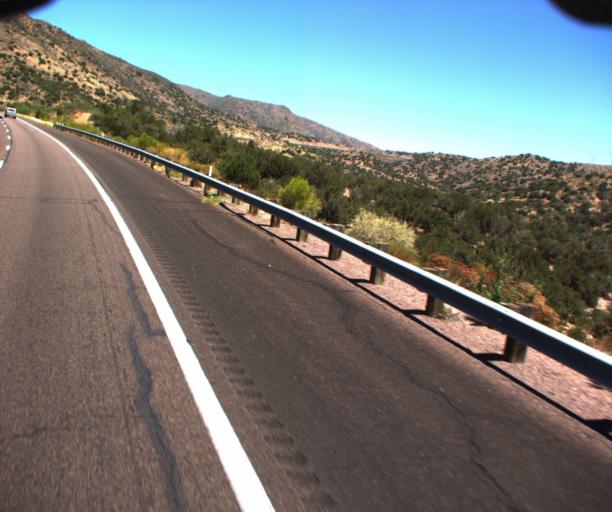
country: US
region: Arizona
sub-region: Gila County
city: Tonto Basin
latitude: 33.9752
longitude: -111.3841
